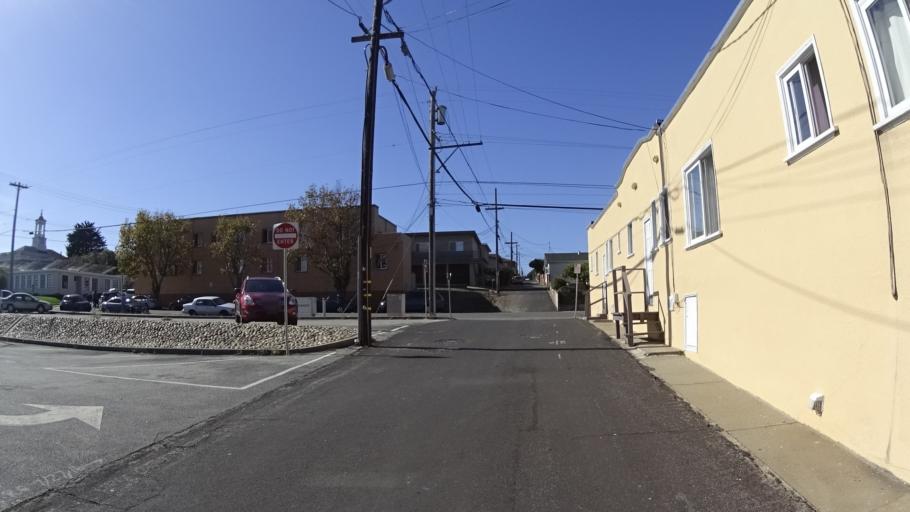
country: US
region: California
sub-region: San Mateo County
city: South San Francisco
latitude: 37.6571
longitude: -122.4116
